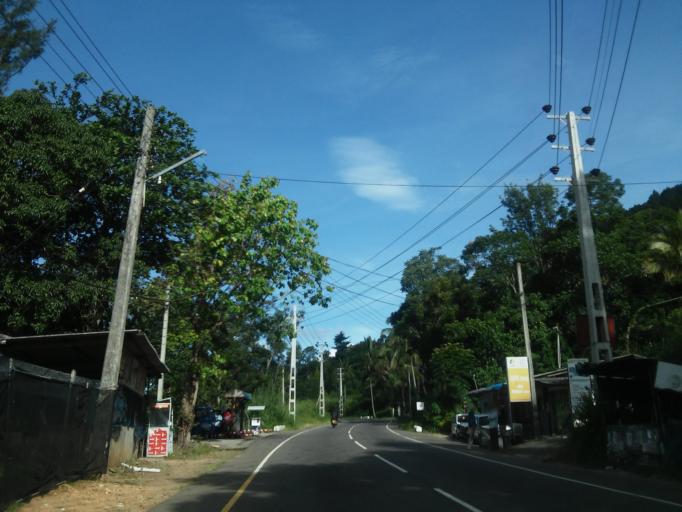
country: LK
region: Uva
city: Haputale
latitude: 6.7615
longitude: 80.8855
